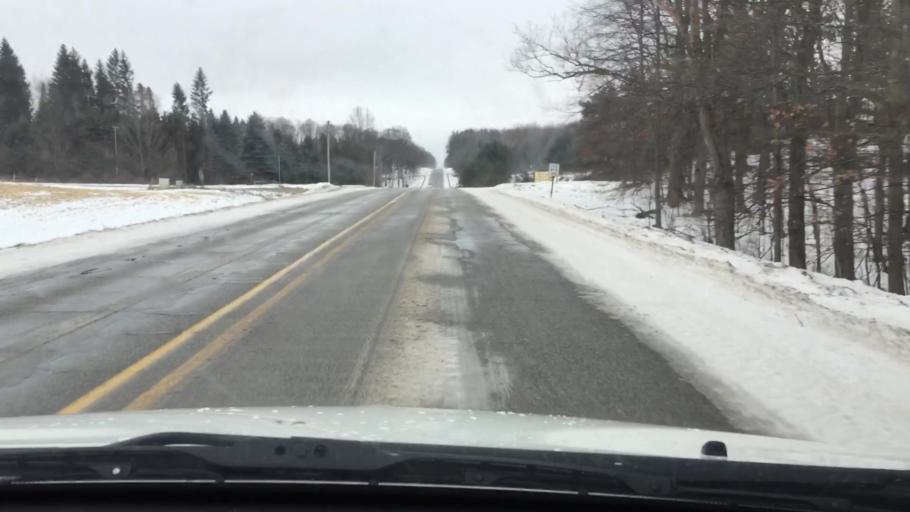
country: US
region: Michigan
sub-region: Wexford County
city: Cadillac
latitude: 44.1802
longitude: -85.4055
